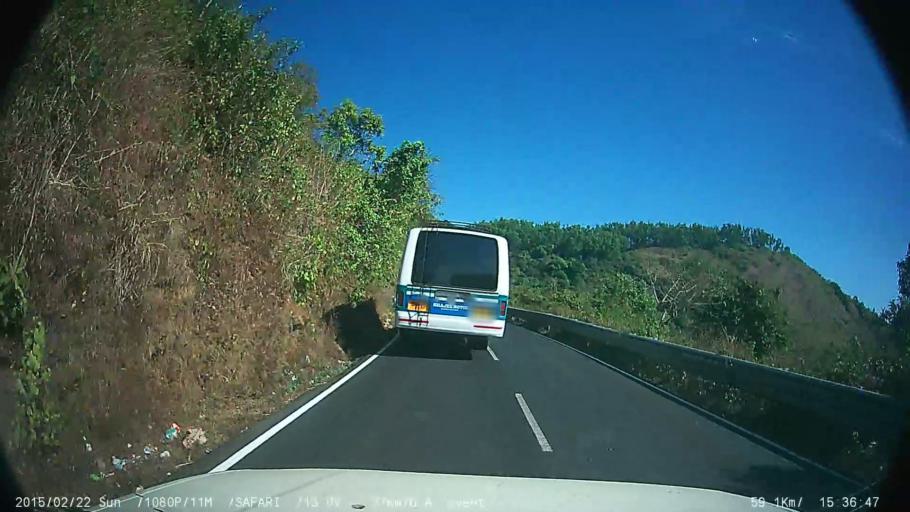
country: IN
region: Kerala
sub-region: Kottayam
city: Erattupetta
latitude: 9.5610
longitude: 76.9799
